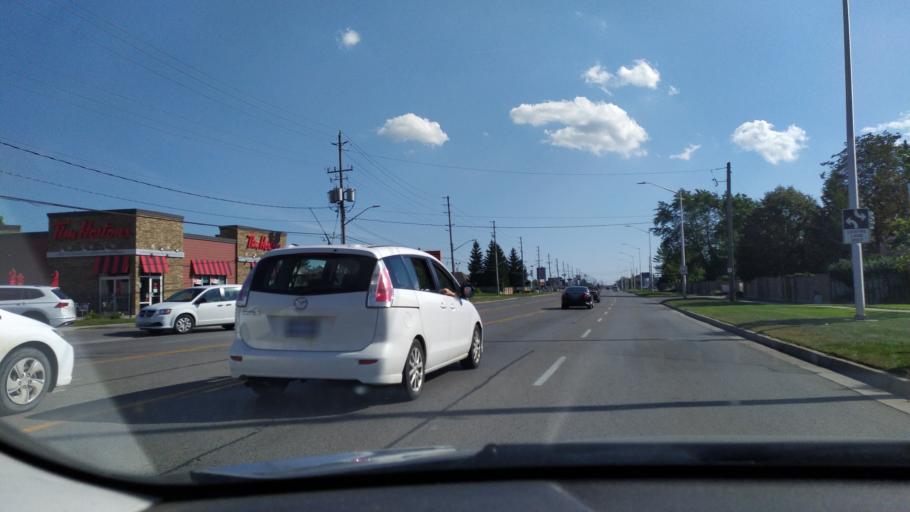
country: CA
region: Ontario
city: London
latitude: 42.9529
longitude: -81.2597
